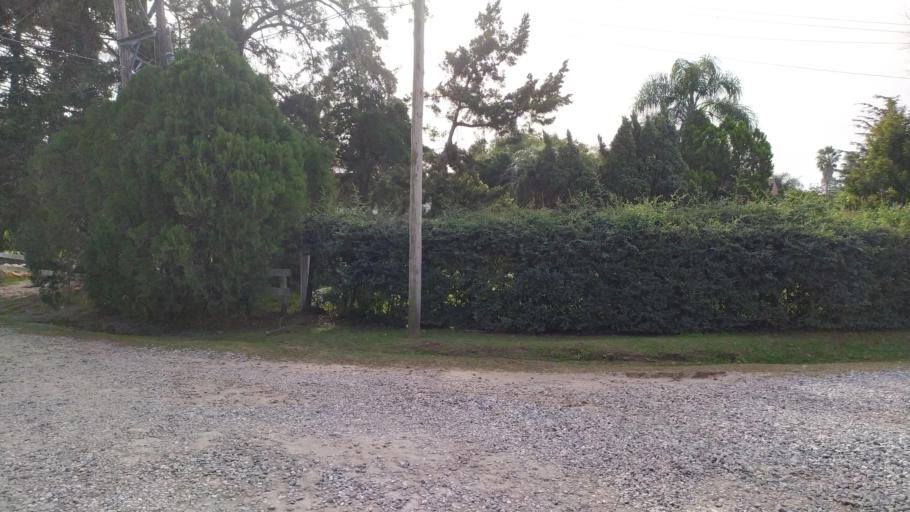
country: AR
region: Santa Fe
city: Santo Tome
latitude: -31.6271
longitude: -60.7594
